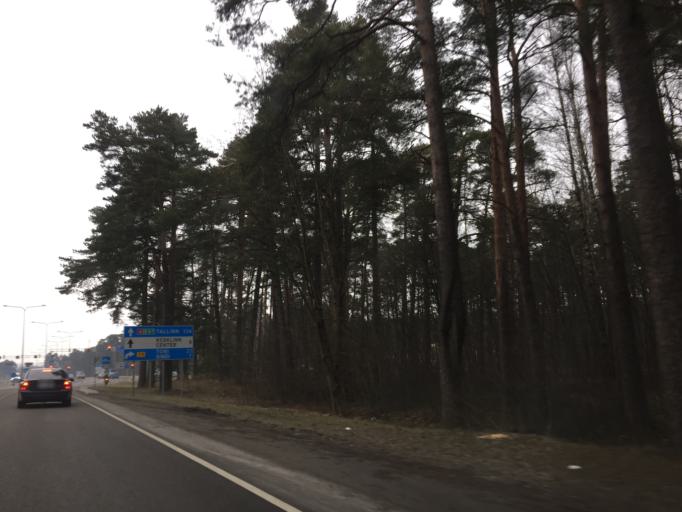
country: EE
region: Paernumaa
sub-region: Paikuse vald
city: Paikuse
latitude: 58.3560
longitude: 24.5759
